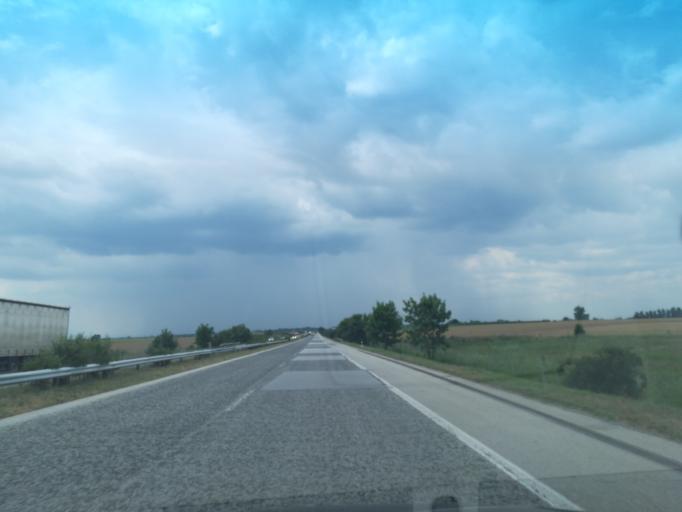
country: BG
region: Stara Zagora
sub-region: Obshtina Chirpan
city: Chirpan
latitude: 42.1929
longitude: 25.1827
